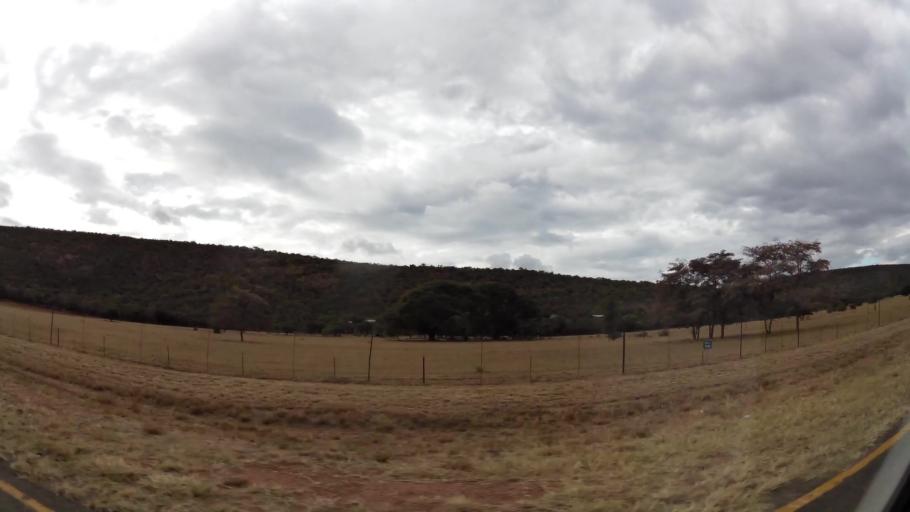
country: ZA
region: Limpopo
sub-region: Waterberg District Municipality
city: Modimolle
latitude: -24.6707
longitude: 28.4936
